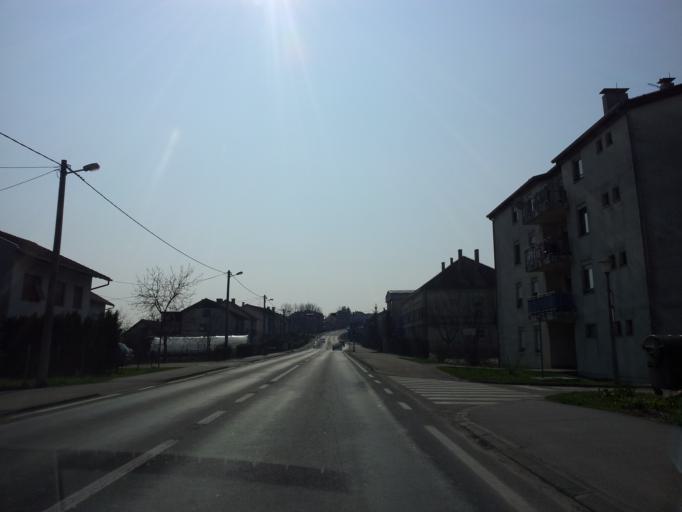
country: HR
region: Karlovacka
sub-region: Grad Karlovac
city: Karlovac
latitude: 45.4617
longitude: 15.5690
